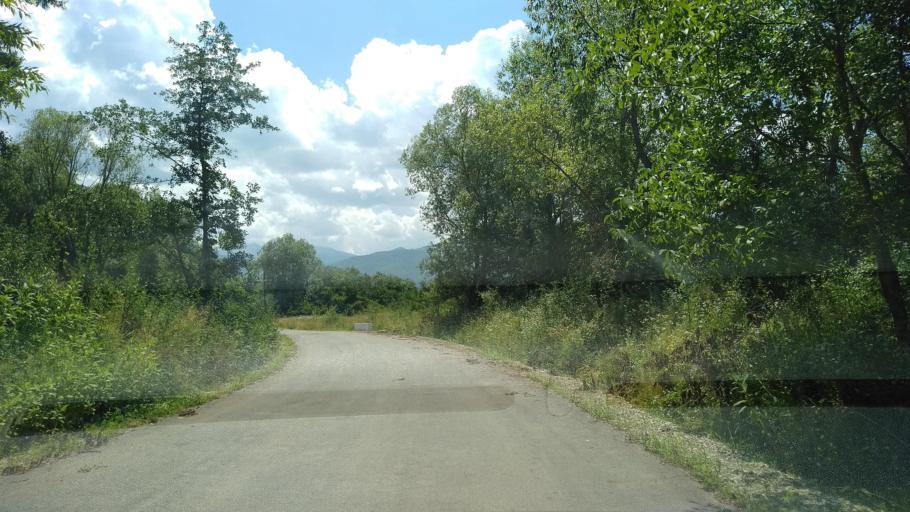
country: RO
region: Hunedoara
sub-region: Comuna Sarmizegetusa
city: Sarmizegetusa
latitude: 45.5339
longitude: 22.8183
